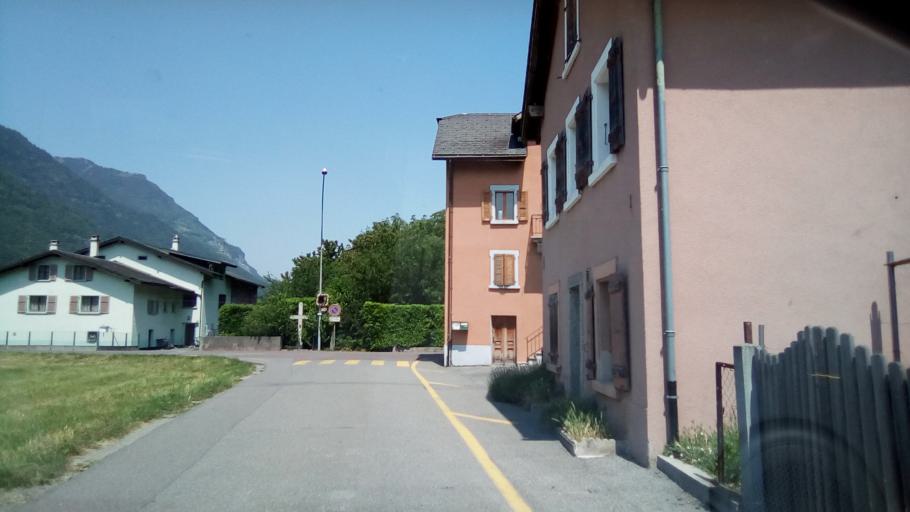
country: CH
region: Valais
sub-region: Saint-Maurice District
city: Vernayaz
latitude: 46.1464
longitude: 7.0436
